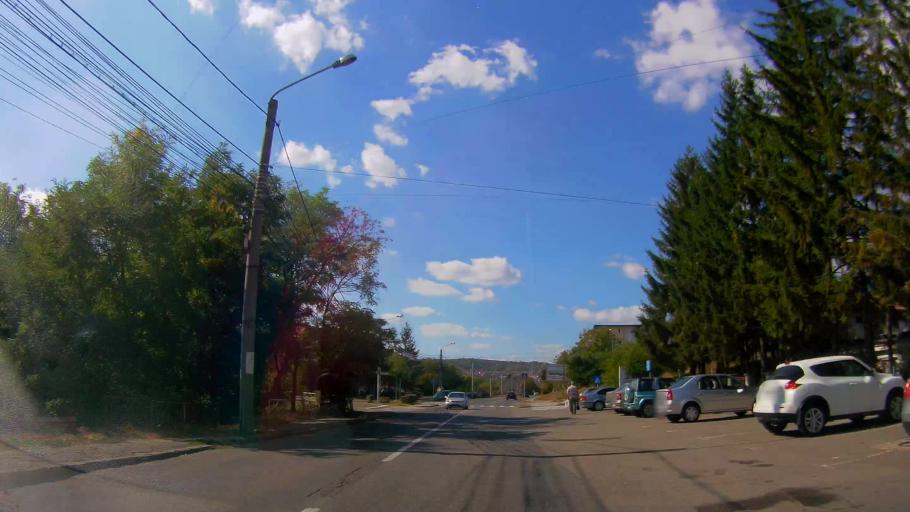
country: RO
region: Salaj
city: Zalau
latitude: 47.1745
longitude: 23.0700
